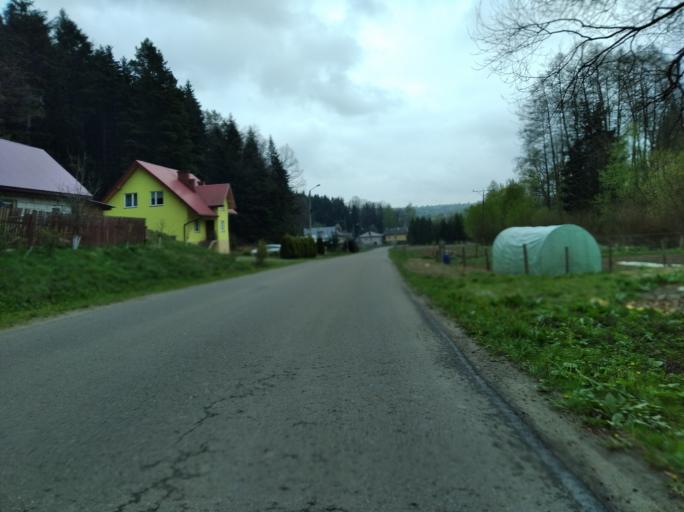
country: PL
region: Subcarpathian Voivodeship
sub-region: Powiat brzozowski
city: Jablonka
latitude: 49.7421
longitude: 22.0786
